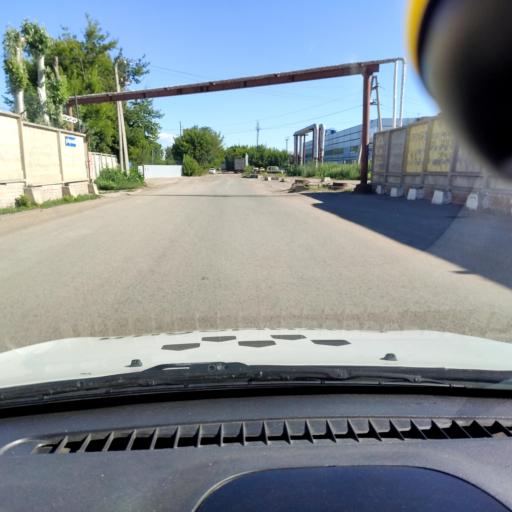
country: RU
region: Samara
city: Tol'yatti
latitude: 53.5862
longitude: 49.2575
